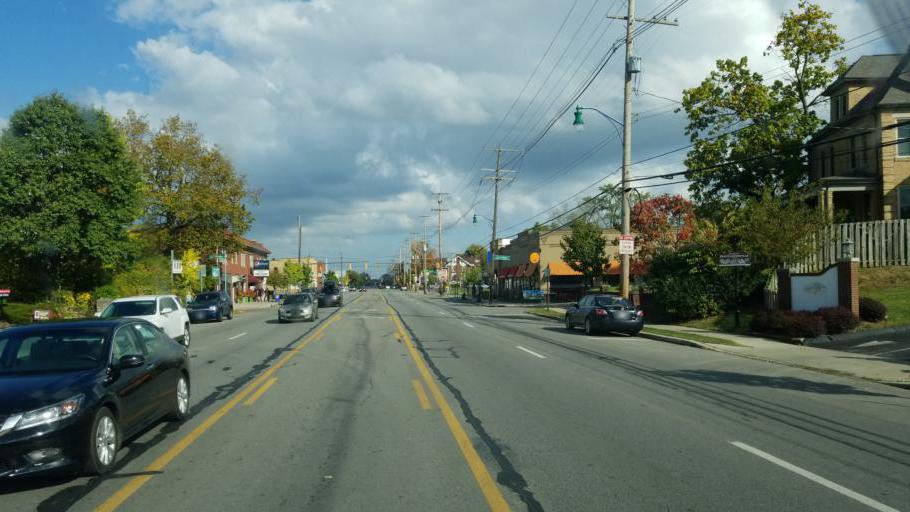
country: US
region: Ohio
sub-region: Franklin County
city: Grandview Heights
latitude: 40.0253
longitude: -83.0142
